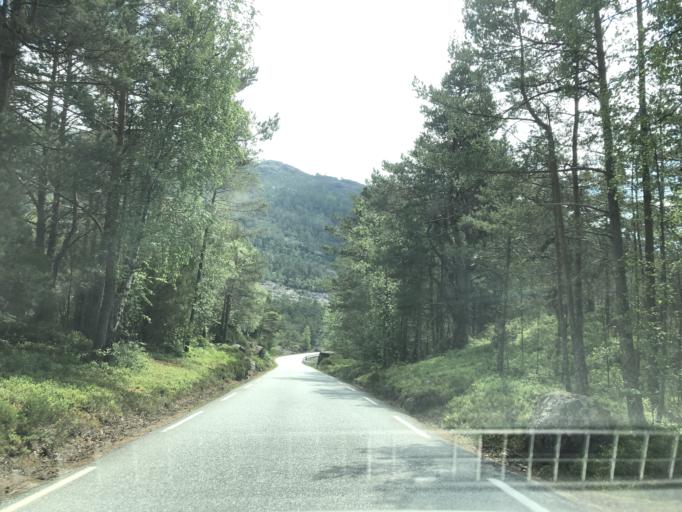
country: NO
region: Hordaland
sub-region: Jondal
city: Jondal
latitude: 60.3277
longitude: 6.3382
